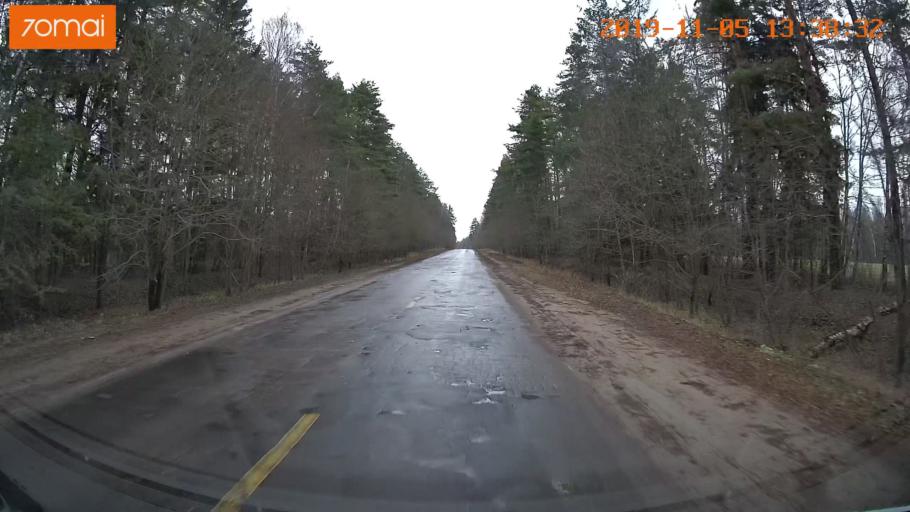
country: RU
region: Ivanovo
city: Shuya
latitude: 56.9327
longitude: 41.3868
